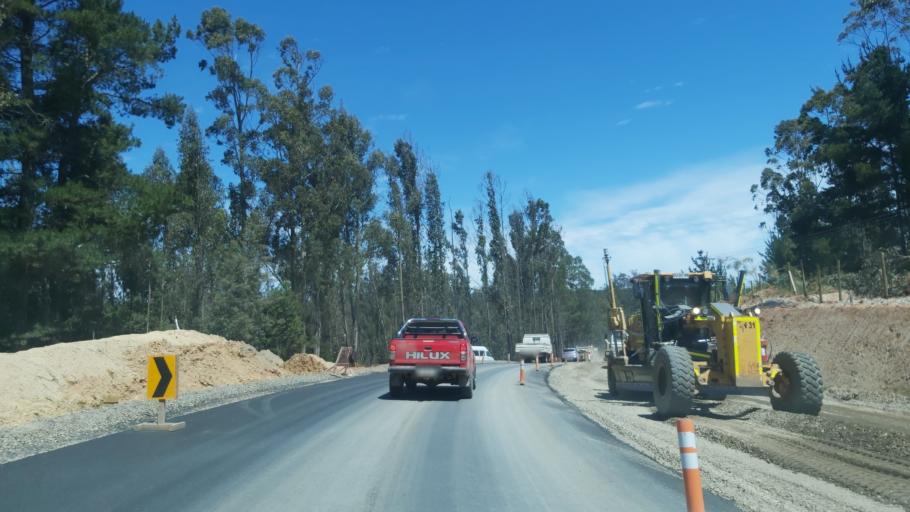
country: CL
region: Maule
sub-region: Provincia de Talca
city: Constitucion
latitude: -35.3845
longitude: -72.4199
